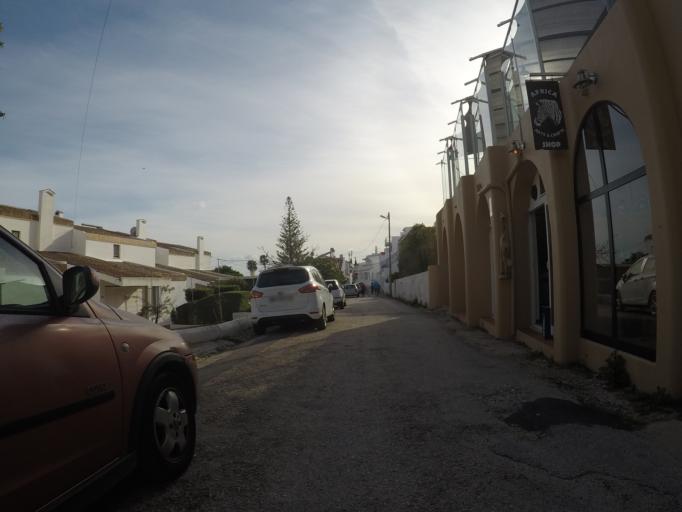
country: PT
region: Faro
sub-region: Lagos
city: Lagos
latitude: 37.0857
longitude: -8.7316
